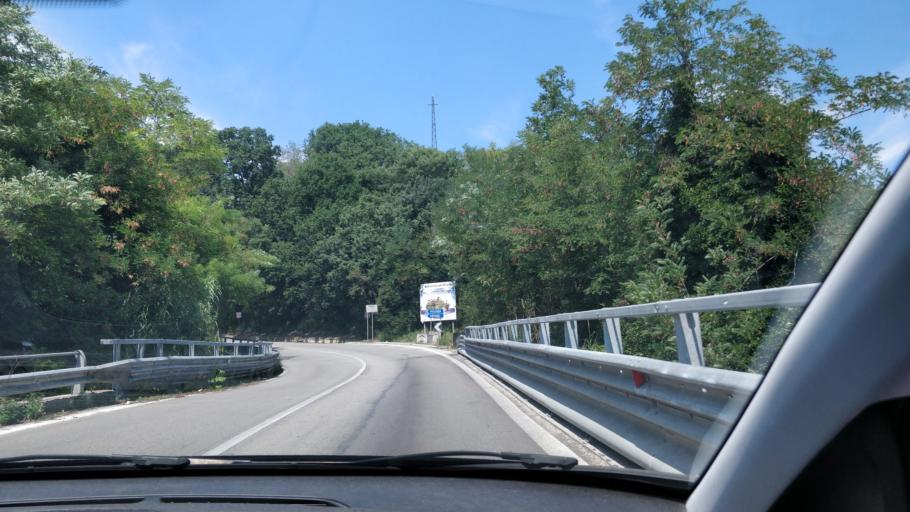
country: IT
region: Abruzzo
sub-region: Provincia di Chieti
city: Ortona
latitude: 42.3448
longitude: 14.4090
